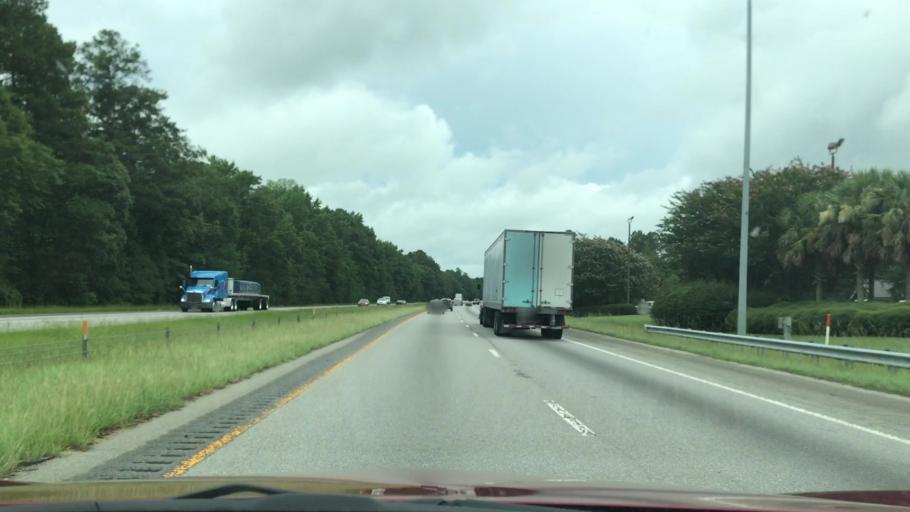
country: US
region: South Carolina
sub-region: Orangeburg County
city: Brookdale
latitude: 33.5015
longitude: -80.7711
